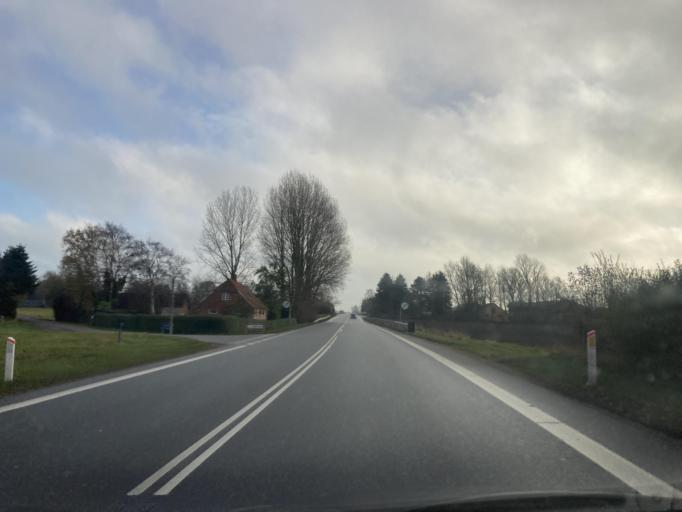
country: DK
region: Zealand
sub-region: Lolland Kommune
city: Maribo
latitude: 54.8128
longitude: 11.4076
